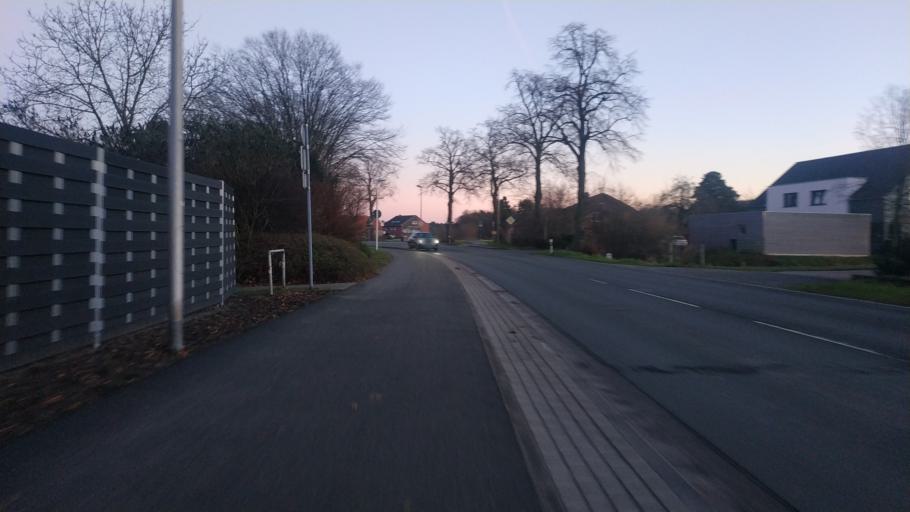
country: DE
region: North Rhine-Westphalia
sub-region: Regierungsbezirk Munster
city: Birgte
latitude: 52.2737
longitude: 7.6732
